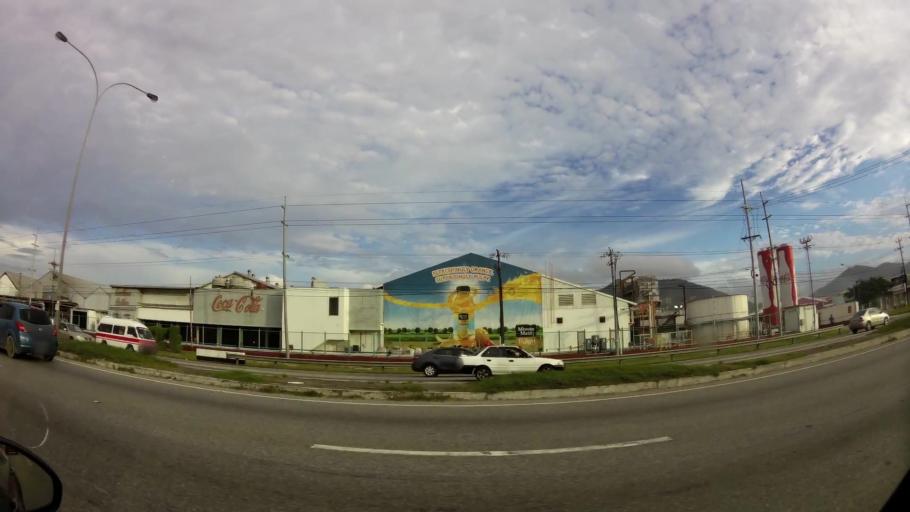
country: TT
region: Tunapuna/Piarco
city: Tunapuna
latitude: 10.6379
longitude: -61.3862
